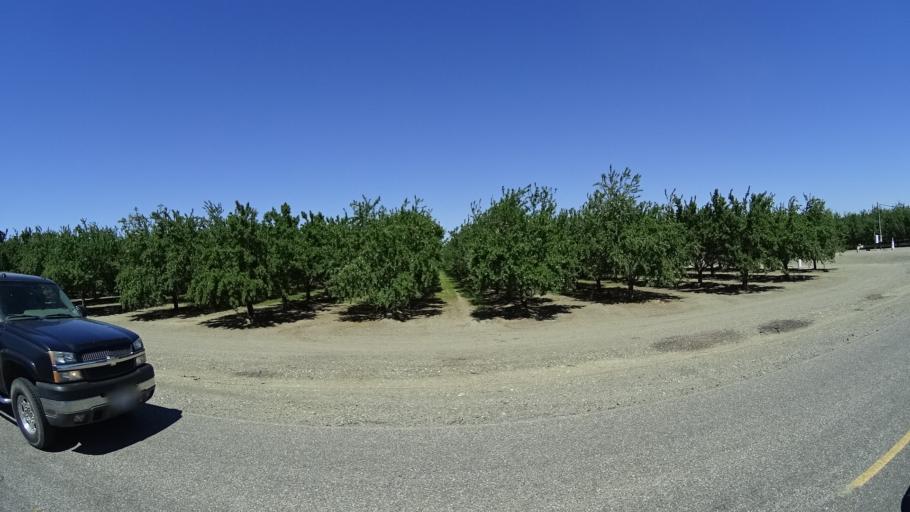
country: US
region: California
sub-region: Glenn County
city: Orland
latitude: 39.7250
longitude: -122.1205
